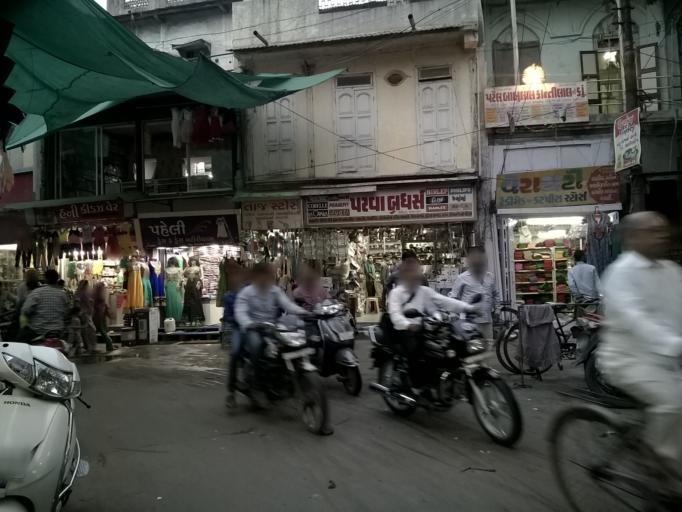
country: IN
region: Gujarat
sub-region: Kheda
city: Nadiad
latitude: 22.6968
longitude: 72.8615
